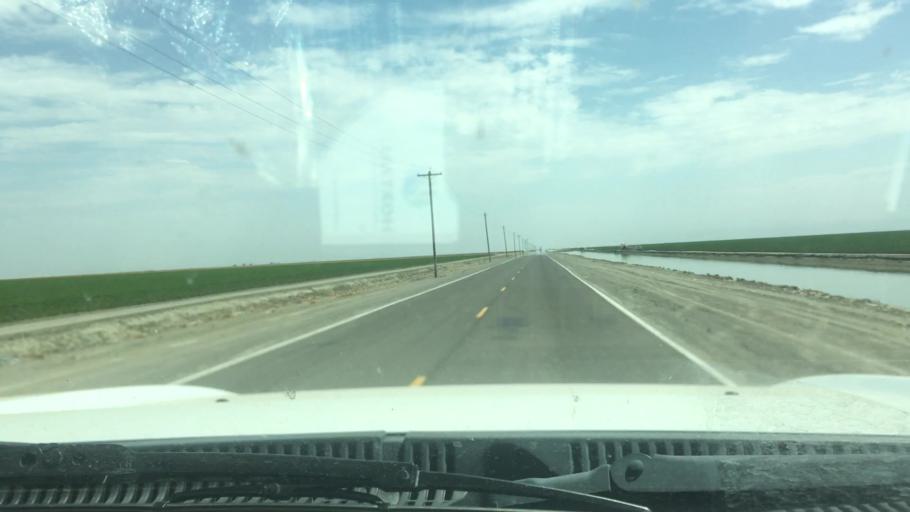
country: US
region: California
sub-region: Tulare County
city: Alpaugh
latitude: 35.9127
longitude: -119.5734
